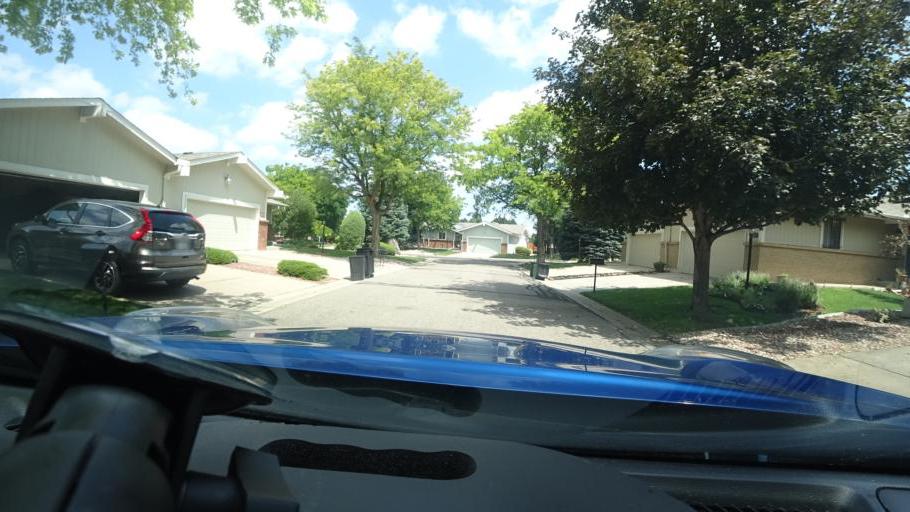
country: US
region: Colorado
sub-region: Adams County
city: Aurora
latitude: 39.7125
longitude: -104.8491
